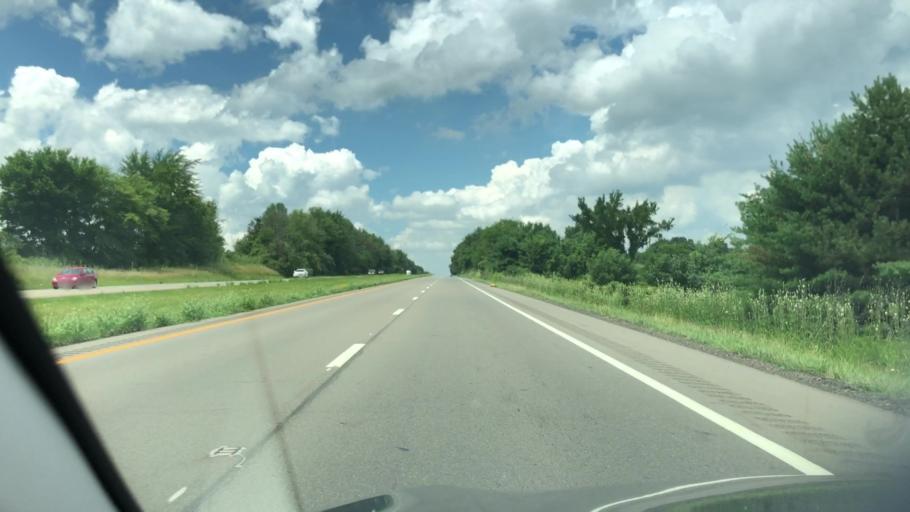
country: US
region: Ohio
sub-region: Stark County
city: Massillon
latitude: 40.8230
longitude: -81.5364
